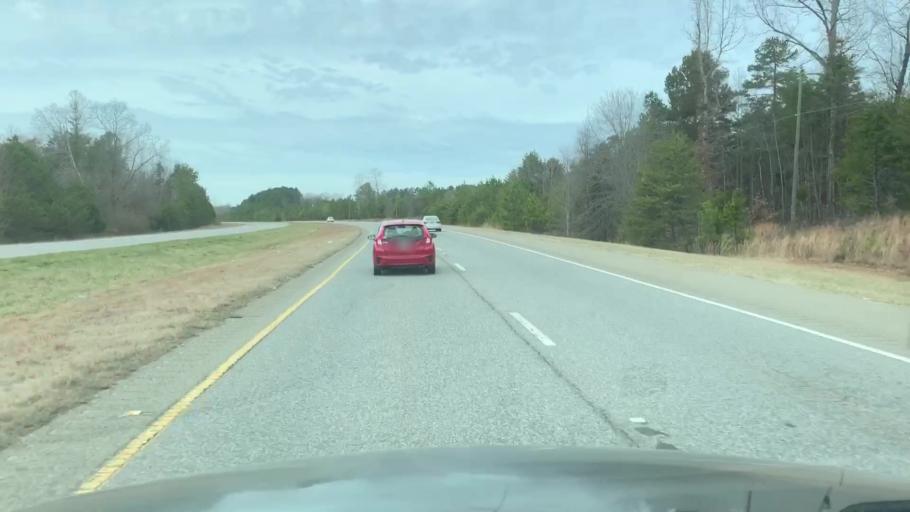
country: US
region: South Carolina
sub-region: Greenville County
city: Golden Grove
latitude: 34.7275
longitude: -82.4048
